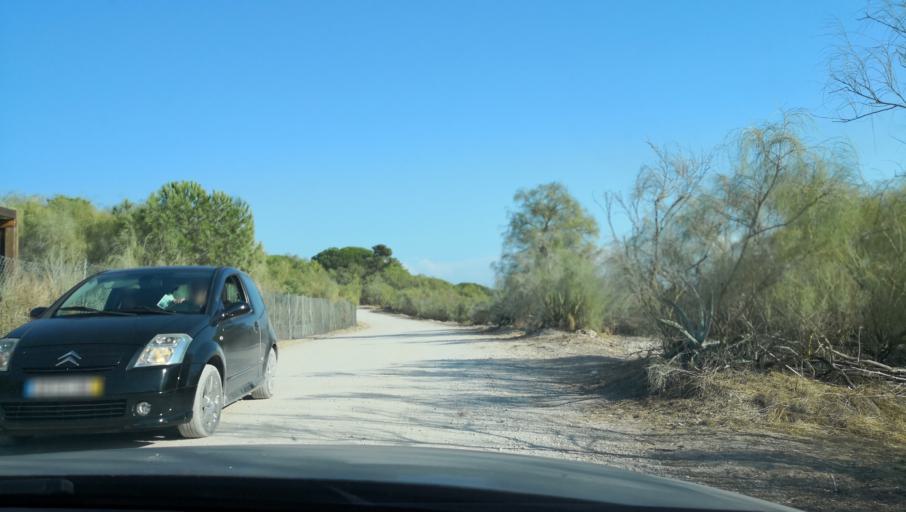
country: PT
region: Setubal
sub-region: Setubal
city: Setubal
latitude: 38.4859
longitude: -8.8854
